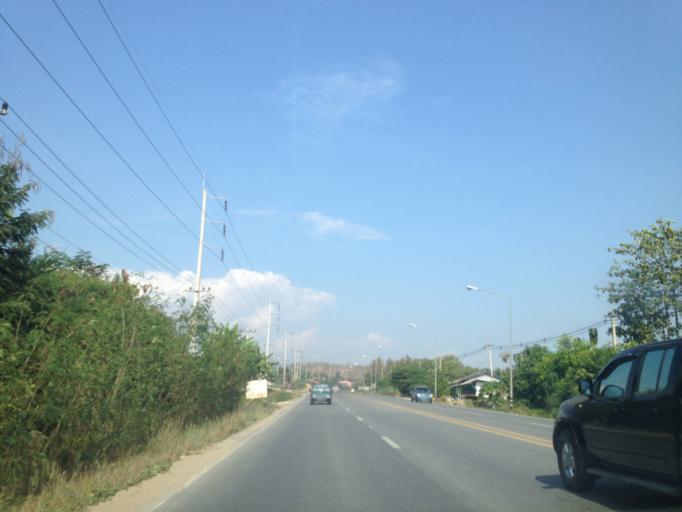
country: TH
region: Chiang Mai
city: Chom Thong
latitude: 18.3492
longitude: 98.6798
